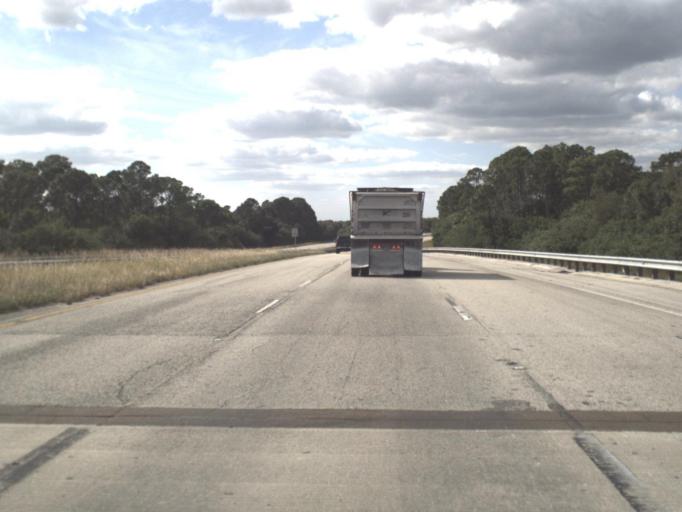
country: US
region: Florida
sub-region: Brevard County
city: Sharpes
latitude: 28.4117
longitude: -80.8266
